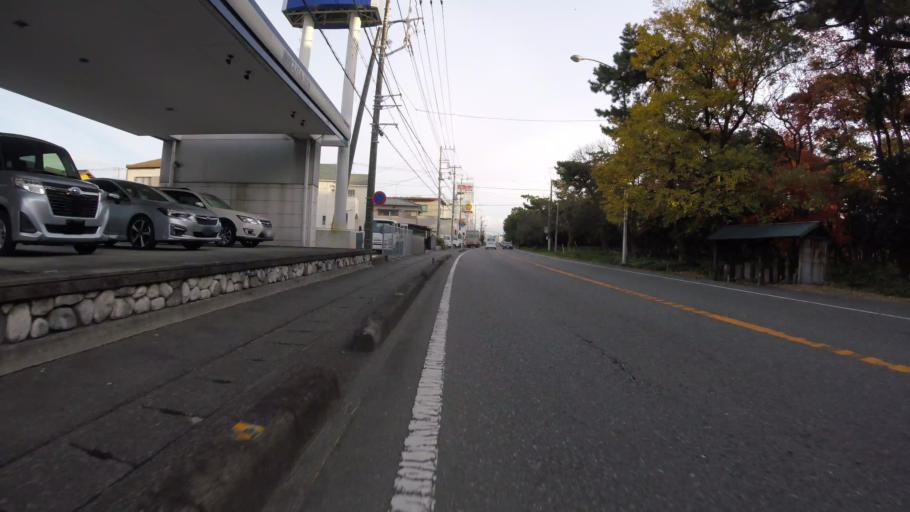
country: JP
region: Shizuoka
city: Numazu
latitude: 35.1049
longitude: 138.8369
